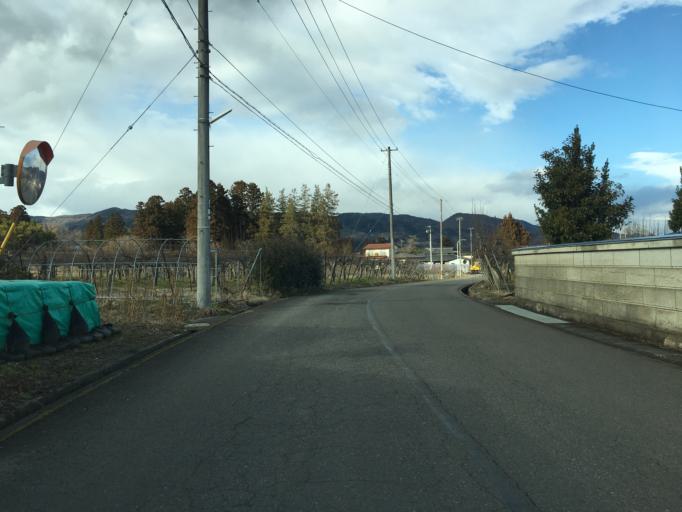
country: JP
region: Fukushima
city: Fukushima-shi
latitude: 37.7534
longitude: 140.3720
